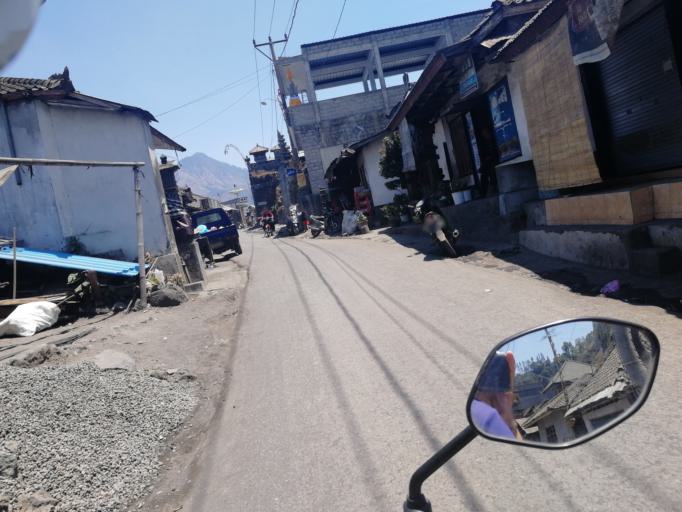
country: ID
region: Bali
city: Banjar Trunyan
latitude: -8.2257
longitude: 115.4094
